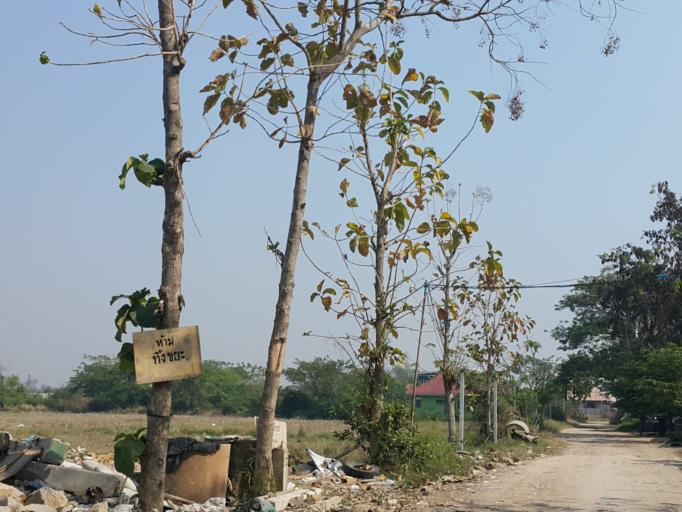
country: TH
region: Chiang Mai
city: San Kamphaeng
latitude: 18.7743
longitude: 99.0762
